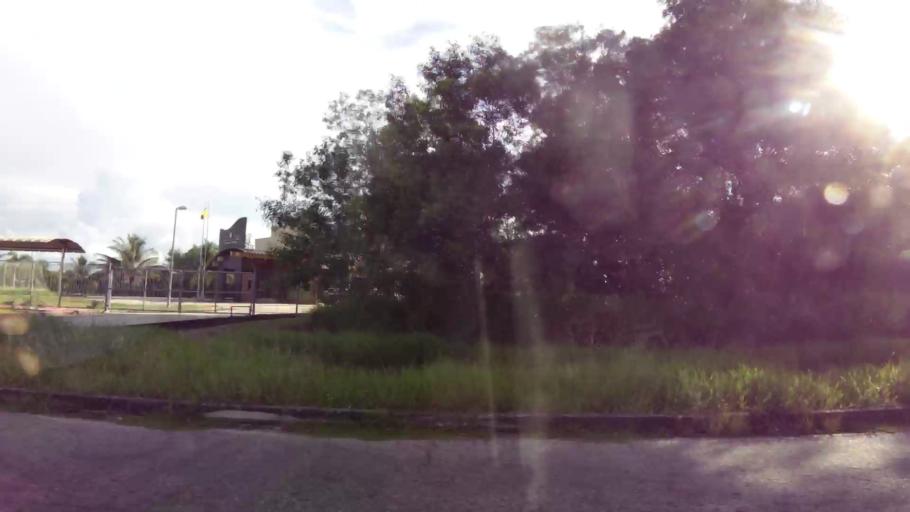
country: BN
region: Brunei and Muara
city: Bandar Seri Begawan
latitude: 4.9843
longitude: 114.9755
